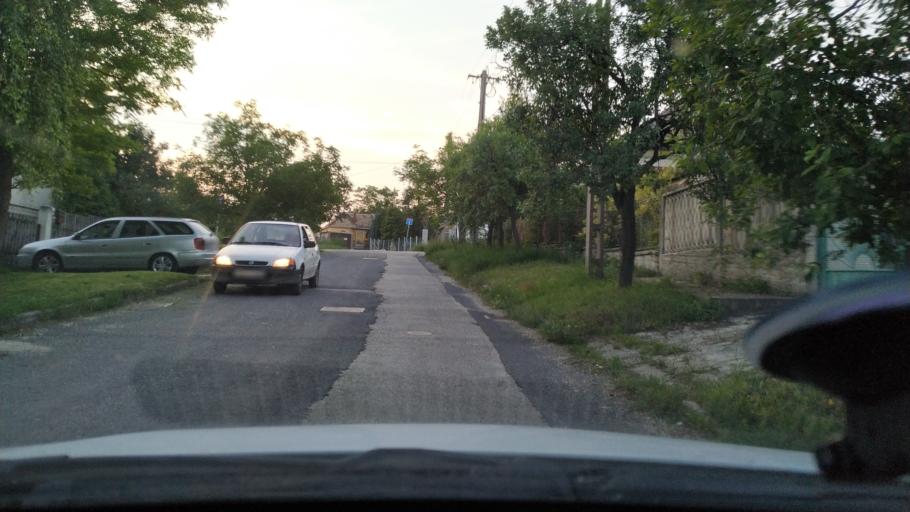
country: HU
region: Veszprem
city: Varpalota
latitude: 47.2039
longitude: 18.1797
